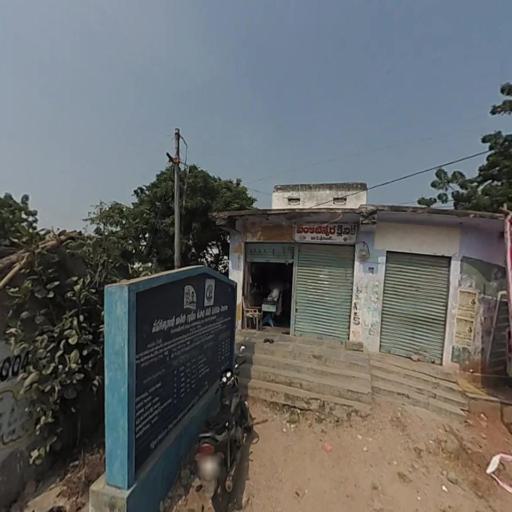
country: IN
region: Telangana
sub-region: Nalgonda
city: Nalgonda
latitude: 17.1864
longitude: 79.1265
